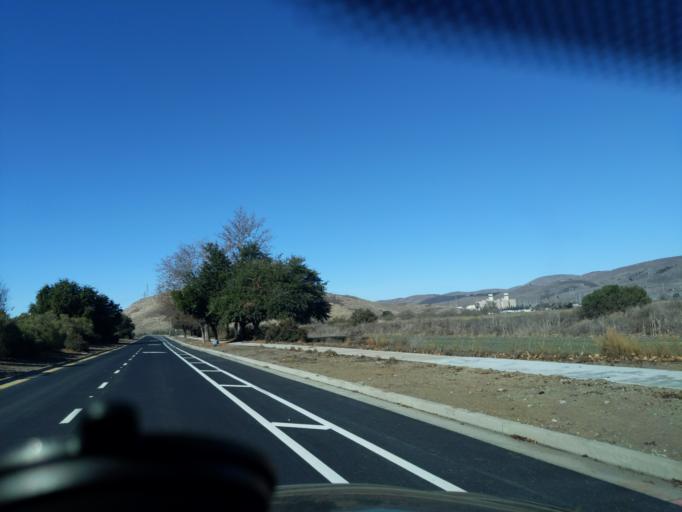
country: US
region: California
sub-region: Santa Clara County
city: Morgan Hill
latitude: 37.2080
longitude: -121.7437
